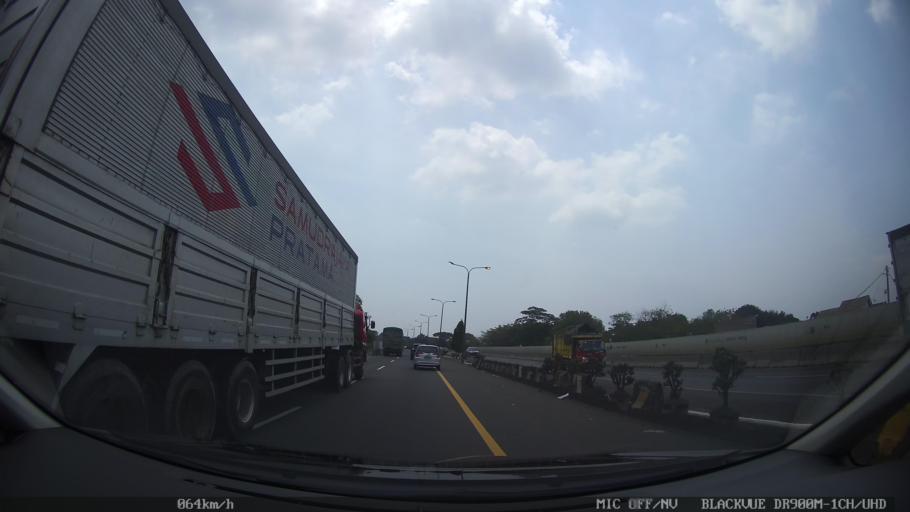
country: ID
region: Banten
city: Serang
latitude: -6.1203
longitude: 106.1892
